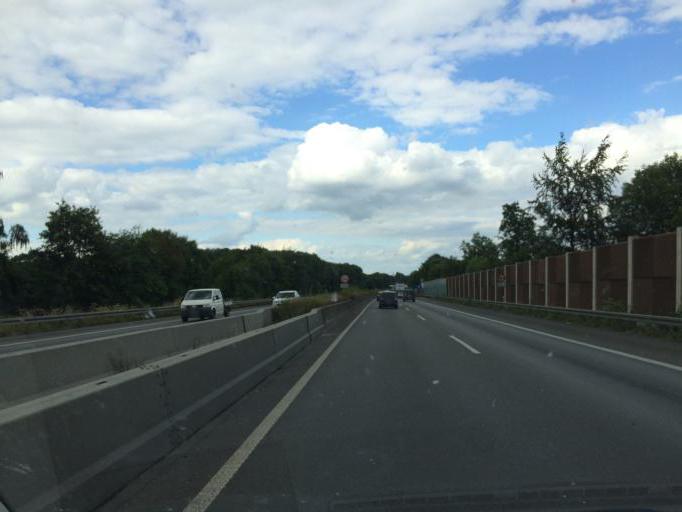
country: DE
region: North Rhine-Westphalia
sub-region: Regierungsbezirk Dusseldorf
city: Rheurdt
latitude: 51.4188
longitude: 6.4895
